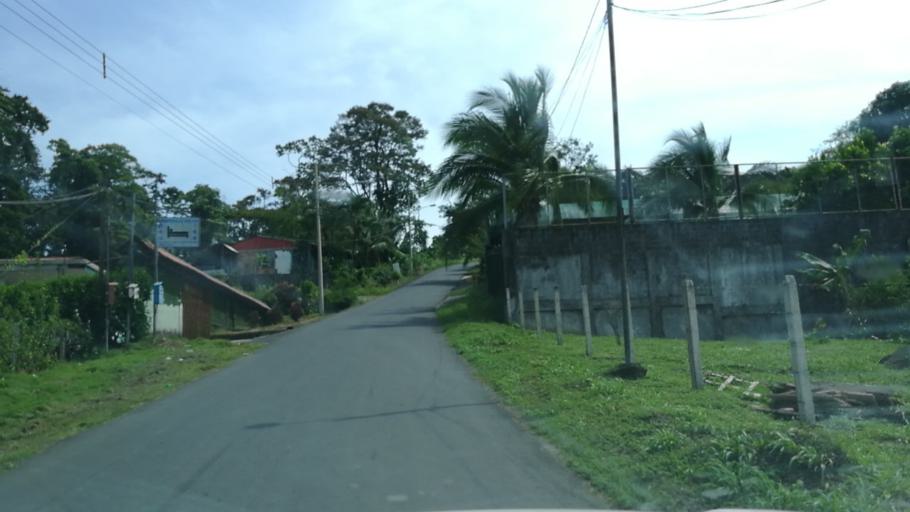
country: CR
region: Limon
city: Limon
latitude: 10.0059
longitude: -83.0575
